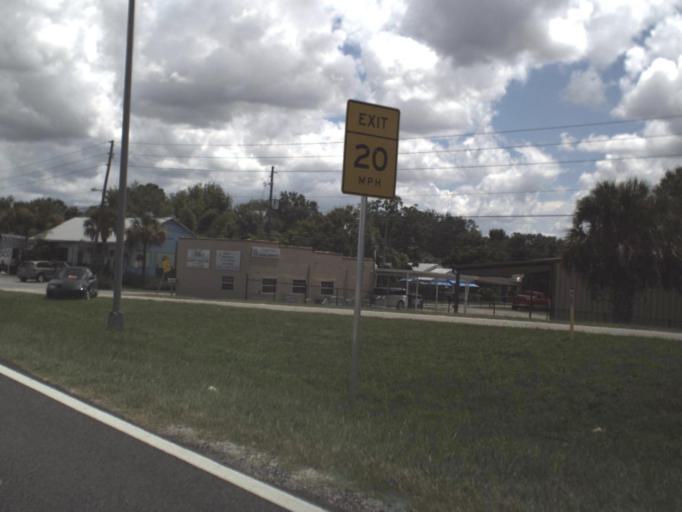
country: US
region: Florida
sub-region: Polk County
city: Lake Wales
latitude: 27.8979
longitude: -81.6026
